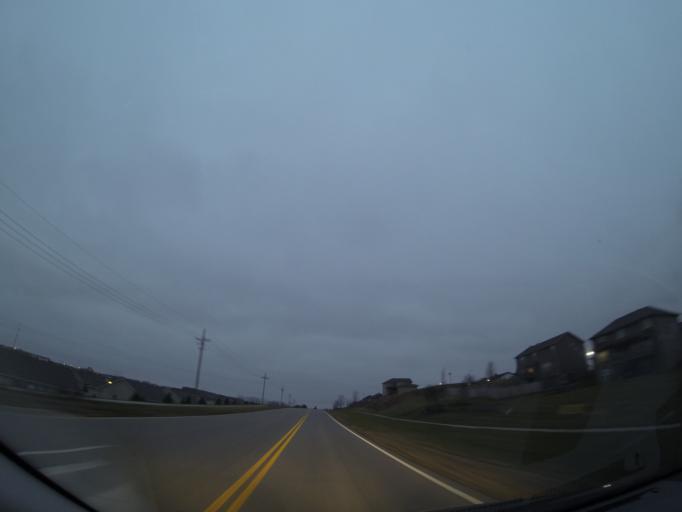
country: US
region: Nebraska
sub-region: Douglas County
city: Elkhorn
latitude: 41.2776
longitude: -96.1869
